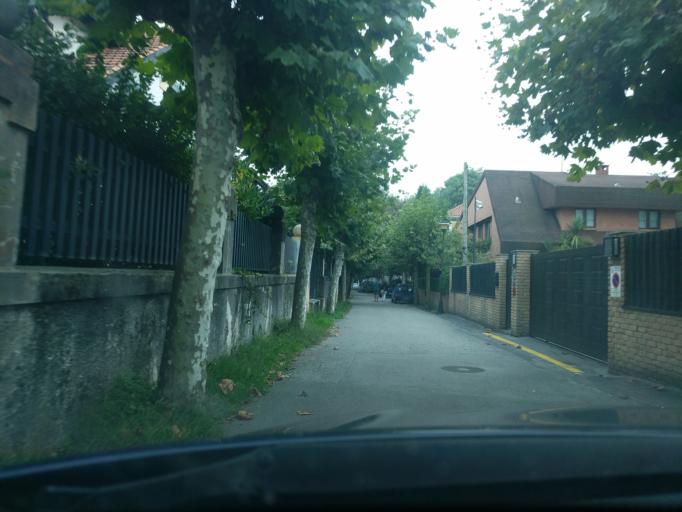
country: ES
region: Asturias
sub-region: Province of Asturias
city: Castrillon
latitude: 43.5757
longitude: -5.9619
